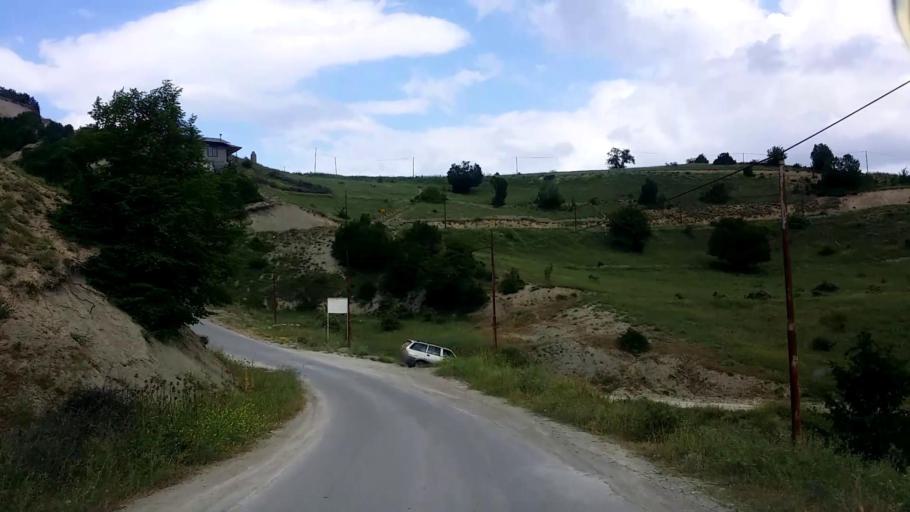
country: IR
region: Mazandaran
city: Chalus
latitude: 36.5535
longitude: 51.2789
